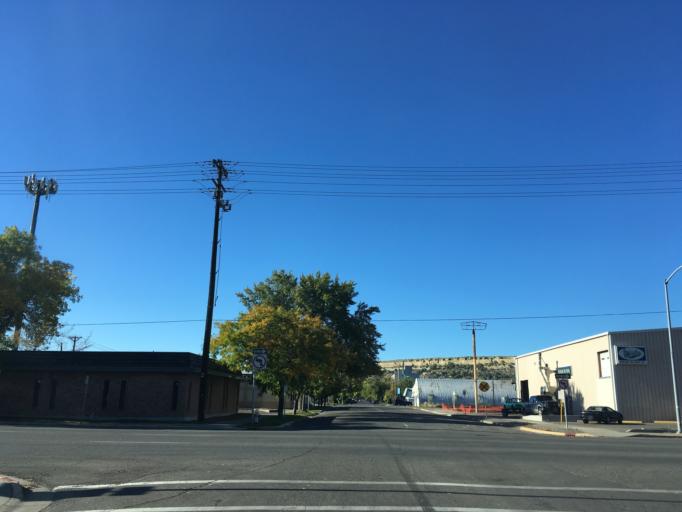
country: US
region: Montana
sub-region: Yellowstone County
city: Billings
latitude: 45.7863
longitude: -108.5045
